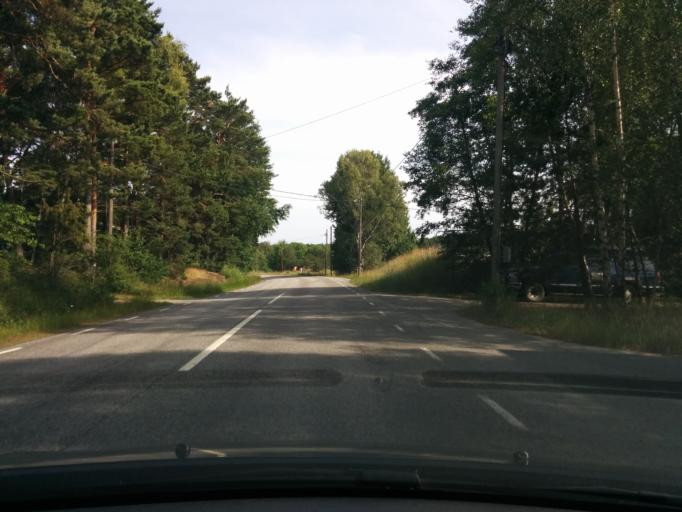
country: SE
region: Stockholm
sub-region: Varmdo Kommun
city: Holo
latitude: 59.3493
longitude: 18.7056
